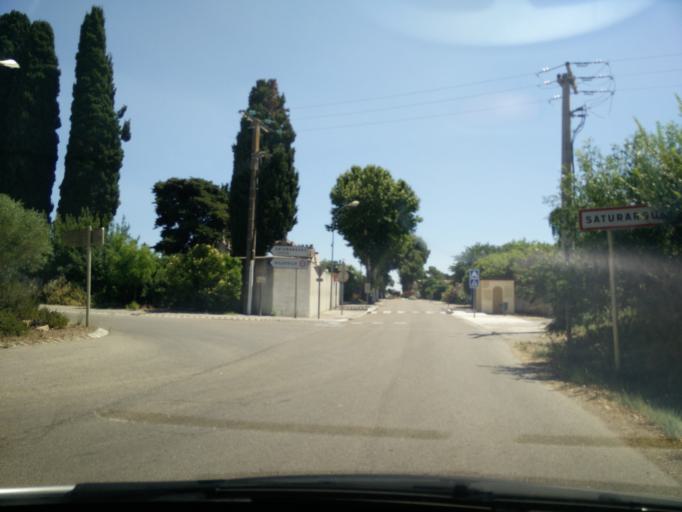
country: FR
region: Languedoc-Roussillon
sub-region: Departement de l'Herault
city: Villetelle
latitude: 43.7227
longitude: 4.1102
